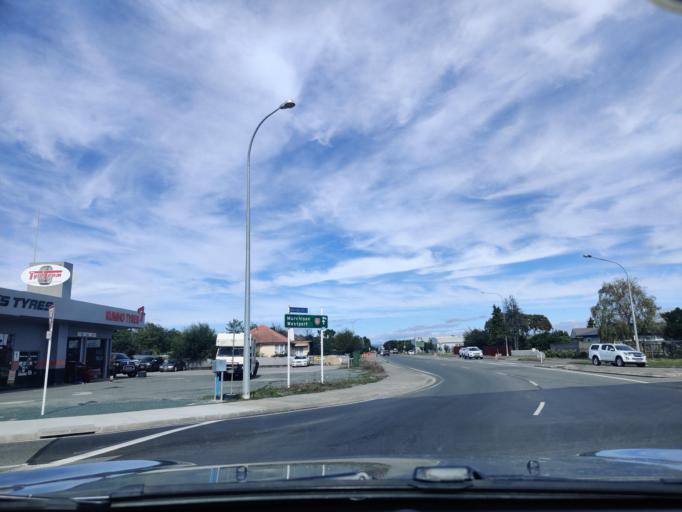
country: NZ
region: Tasman
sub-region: Tasman District
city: Richmond
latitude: -41.3455
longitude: 173.1679
